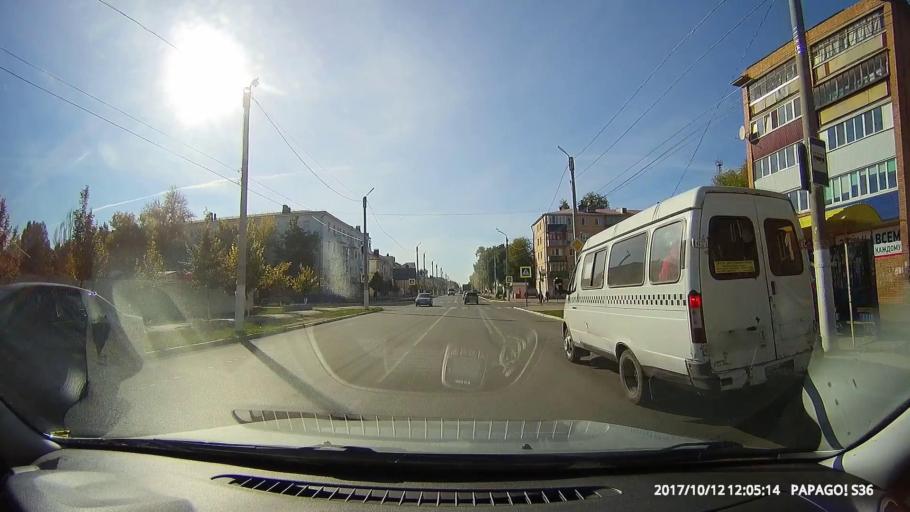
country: RU
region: Samara
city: Chapayevsk
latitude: 52.9781
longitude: 49.7131
